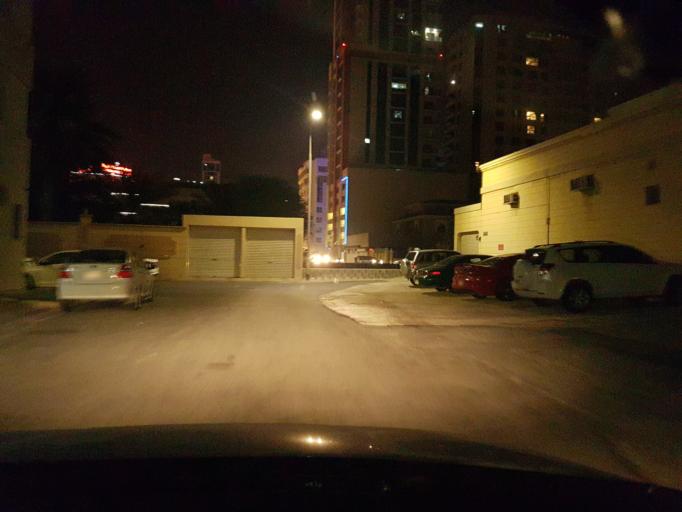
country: BH
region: Manama
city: Manama
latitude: 26.2145
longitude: 50.6028
